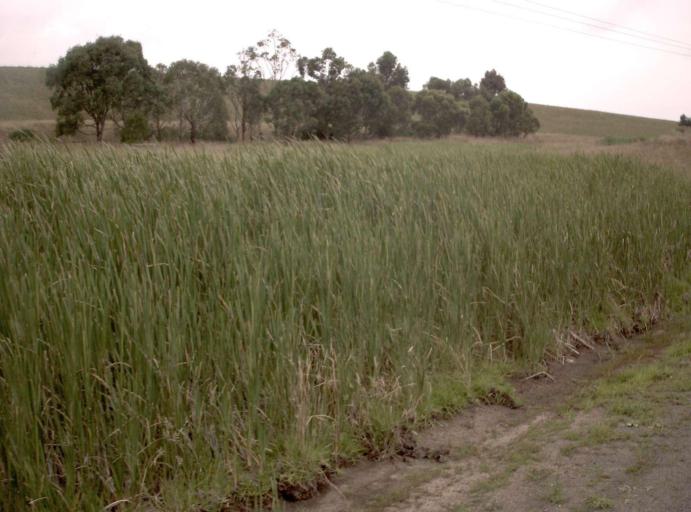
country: AU
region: Victoria
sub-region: Latrobe
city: Morwell
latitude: -38.2827
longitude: 146.3717
